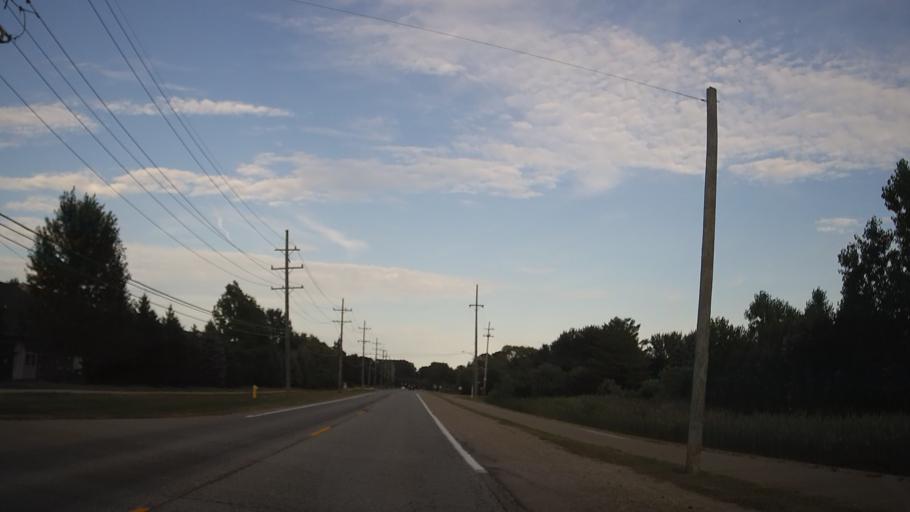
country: US
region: Michigan
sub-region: Macomb County
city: Clinton
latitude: 42.5986
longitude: -82.9259
